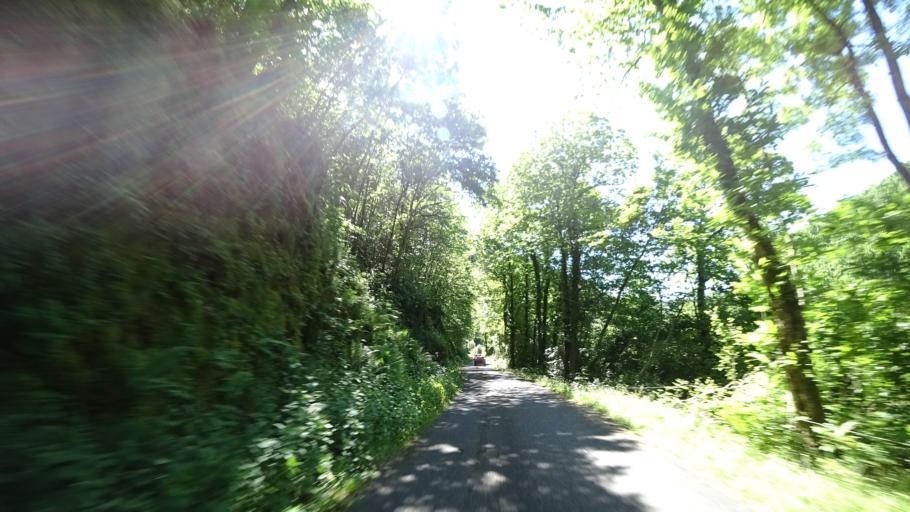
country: FR
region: Midi-Pyrenees
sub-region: Departement de l'Aveyron
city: Colombies
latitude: 44.3763
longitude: 2.3137
